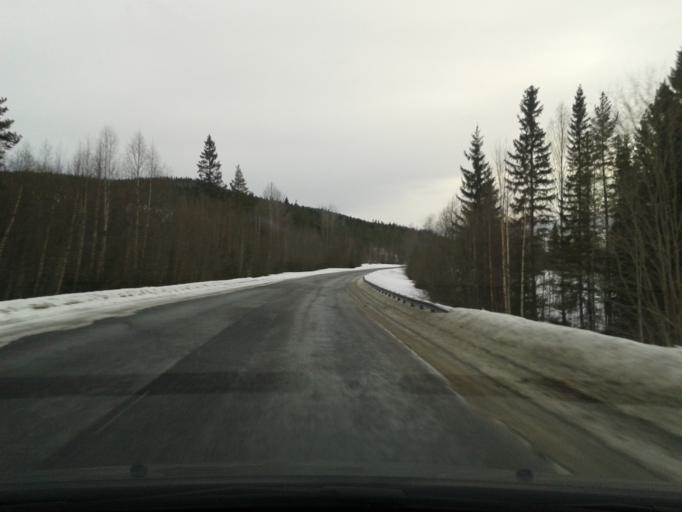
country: SE
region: Vaesternorrland
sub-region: Solleftea Kommun
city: As
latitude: 63.5477
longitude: 16.8448
